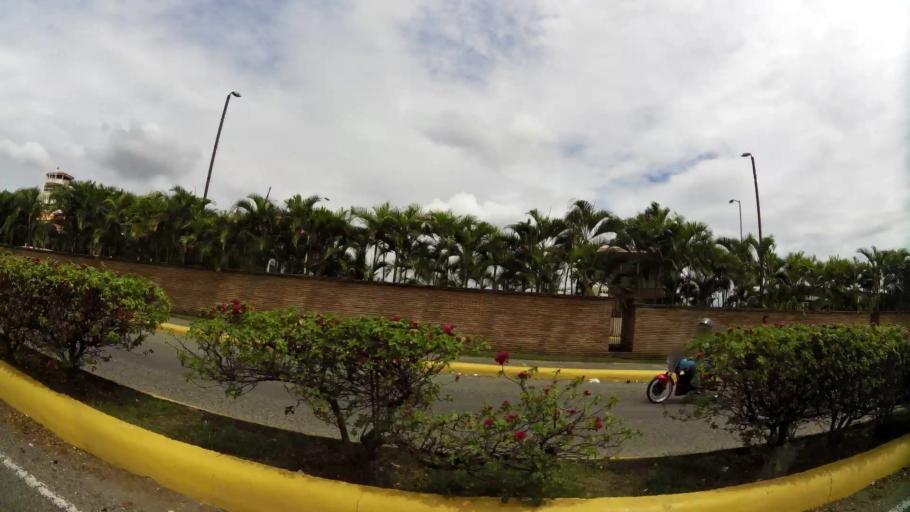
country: DO
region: Santiago
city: Licey al Medio
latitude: 19.4012
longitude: -70.6008
